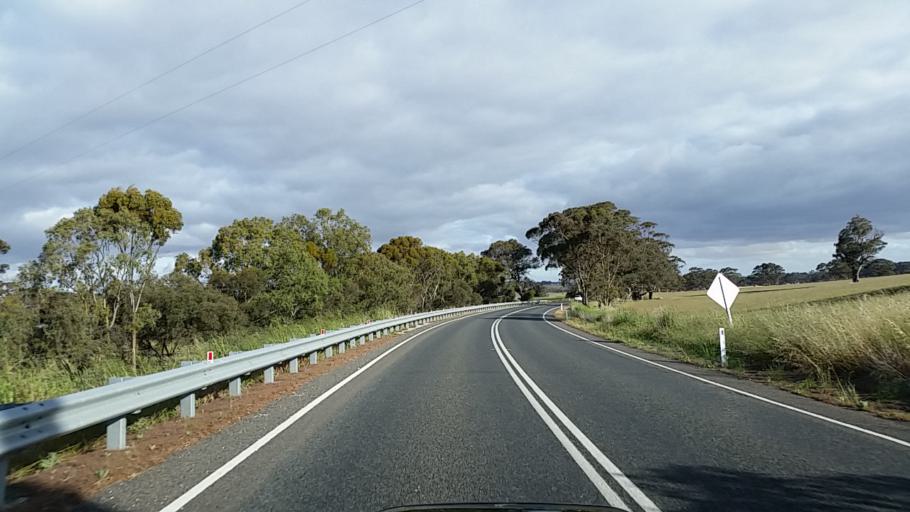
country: AU
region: South Australia
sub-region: Barossa
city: Angaston
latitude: -34.5588
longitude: 139.1465
